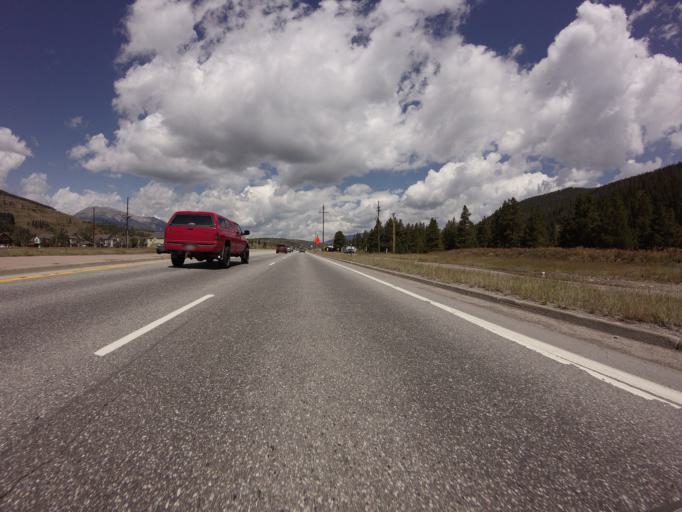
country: US
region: Colorado
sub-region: Summit County
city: Frisco
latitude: 39.5600
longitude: -106.0509
